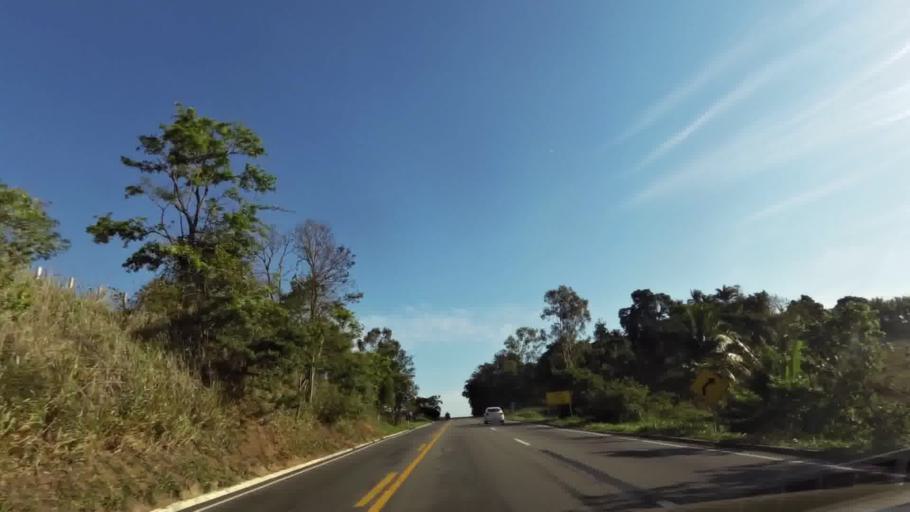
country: BR
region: Espirito Santo
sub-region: Viana
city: Viana
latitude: -20.4956
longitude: -40.4764
